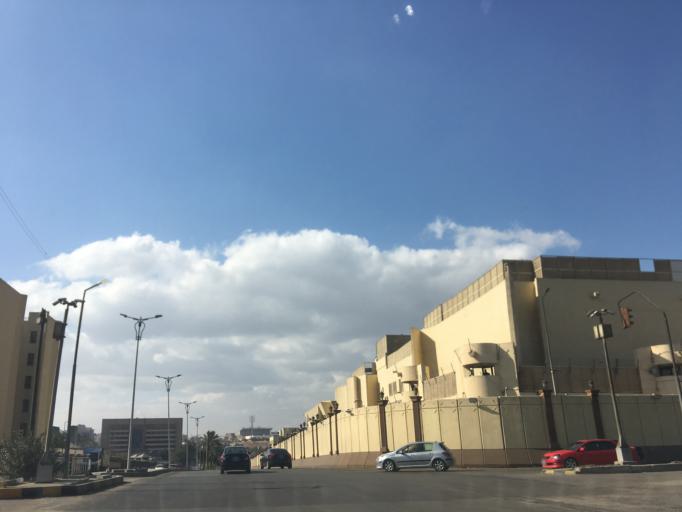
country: EG
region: Muhafazat al Qahirah
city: Cairo
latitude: 30.0507
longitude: 31.3122
